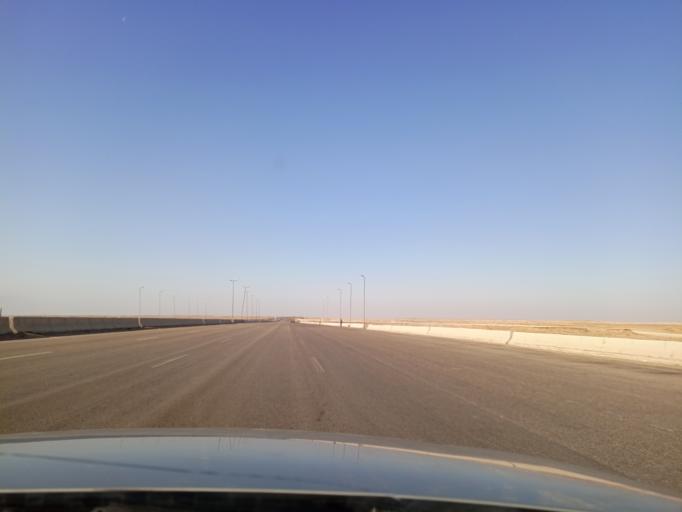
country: EG
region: Muhafazat al Fayyum
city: Tamiyah
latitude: 29.6268
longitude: 30.9619
